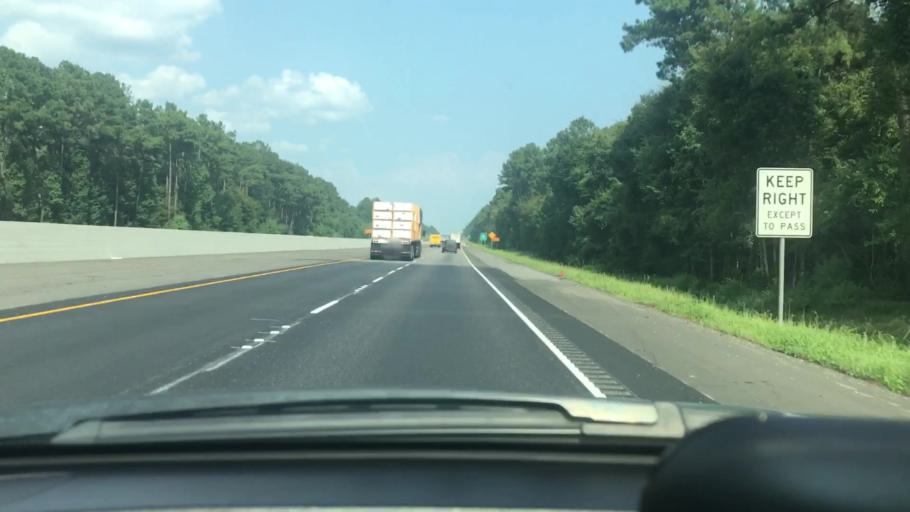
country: US
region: Louisiana
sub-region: Livingston Parish
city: Albany
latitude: 30.4745
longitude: -90.6581
